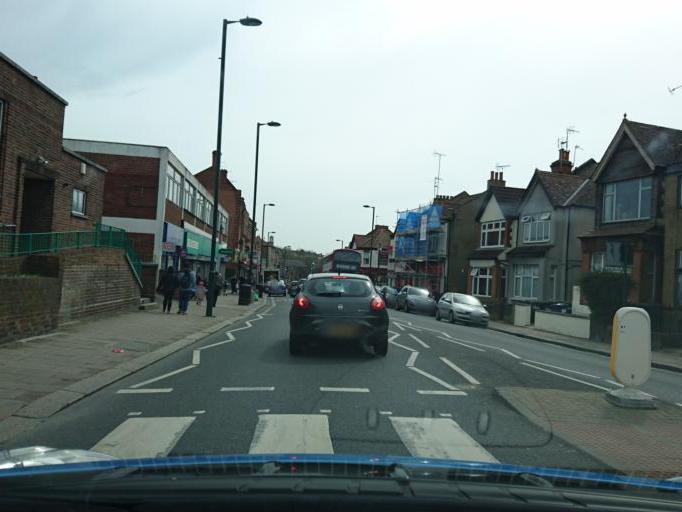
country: GB
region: England
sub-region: Greater London
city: Hadley Wood
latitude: 51.6433
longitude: -0.1652
